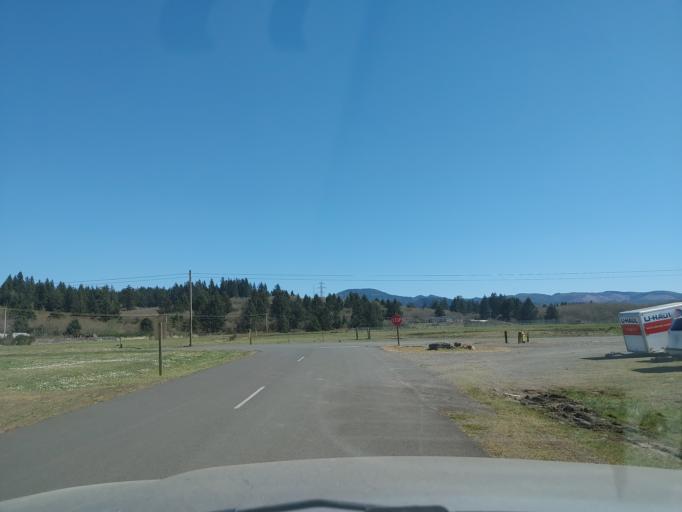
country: US
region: Oregon
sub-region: Tillamook County
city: Tillamook
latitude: 45.4190
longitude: -123.8024
